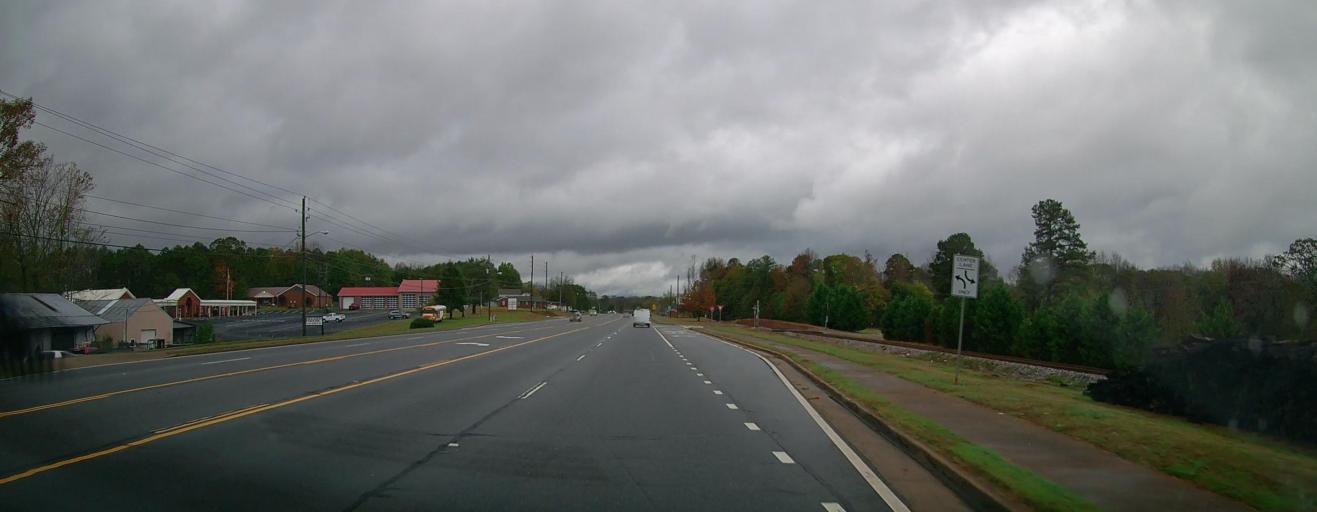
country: US
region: Georgia
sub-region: Jackson County
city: Nicholson
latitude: 34.1068
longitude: -83.4334
